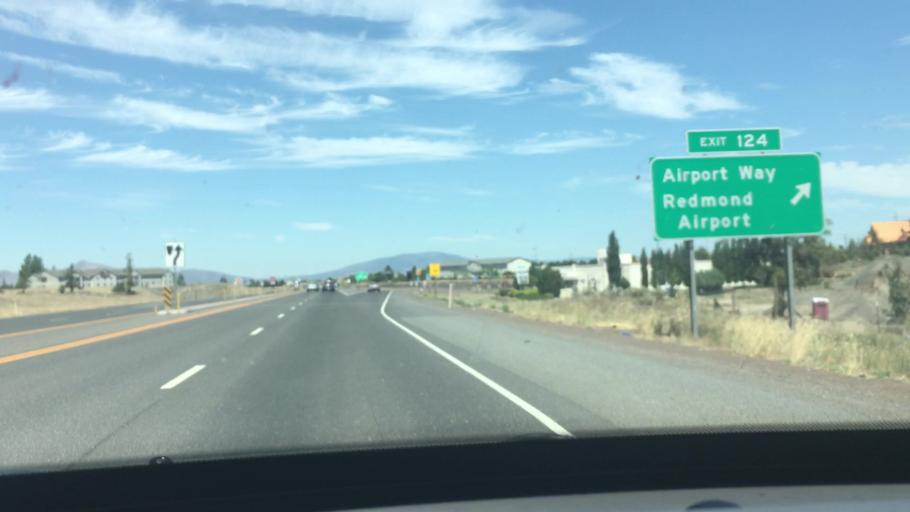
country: US
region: Oregon
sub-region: Deschutes County
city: Redmond
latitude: 44.2393
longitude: -121.1966
